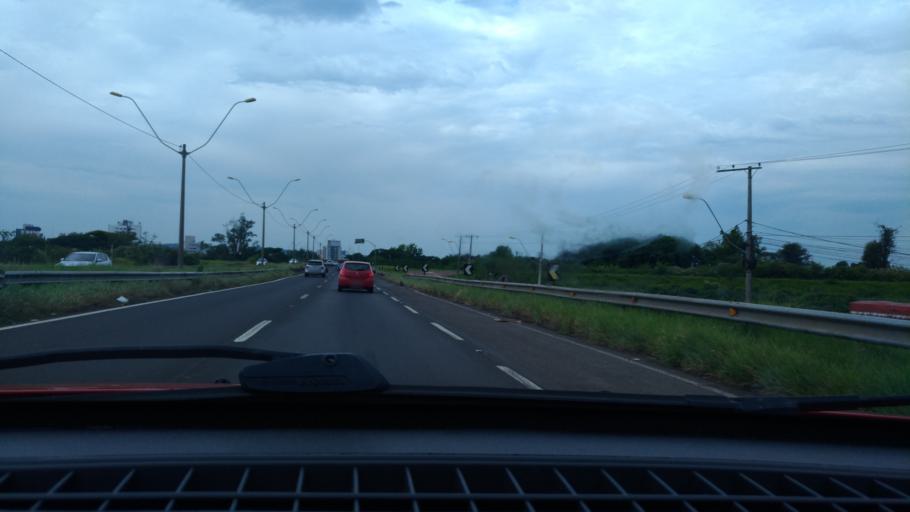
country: BR
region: Rio Grande do Sul
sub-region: Sao Leopoldo
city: Sao Leopoldo
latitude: -29.7560
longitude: -51.1519
